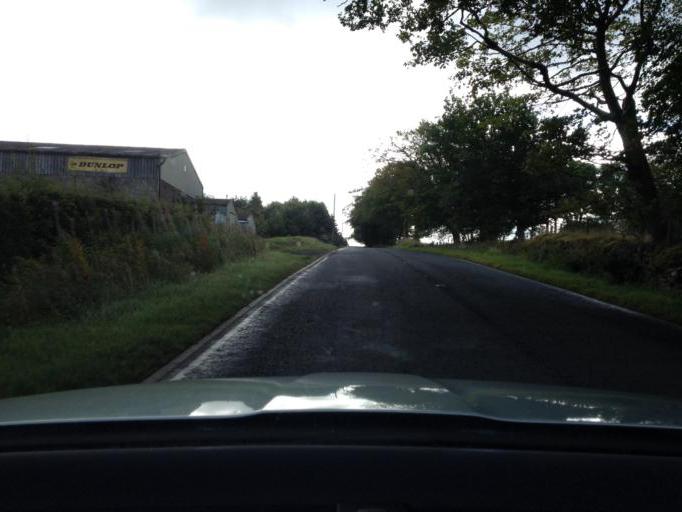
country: GB
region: Scotland
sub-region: West Lothian
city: West Calder
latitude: 55.8244
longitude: -3.5311
